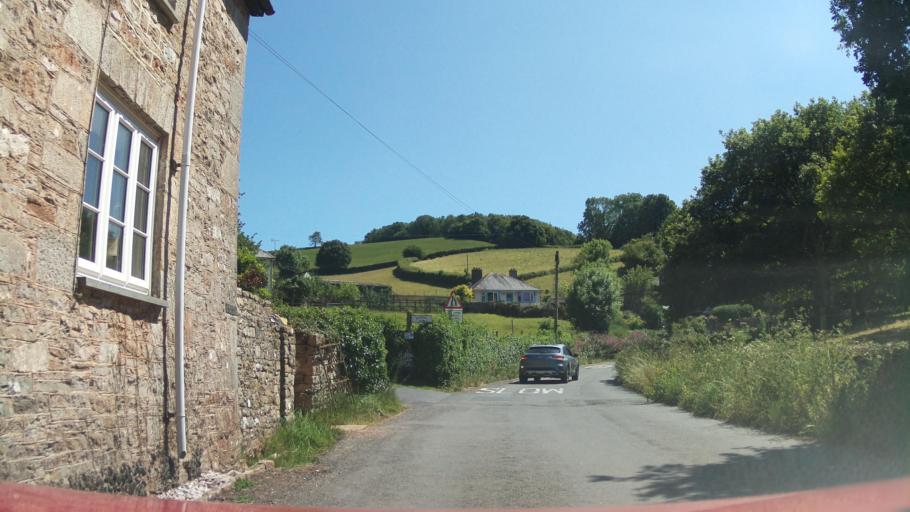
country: GB
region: England
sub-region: Devon
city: Marldon
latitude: 50.4701
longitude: -3.5945
